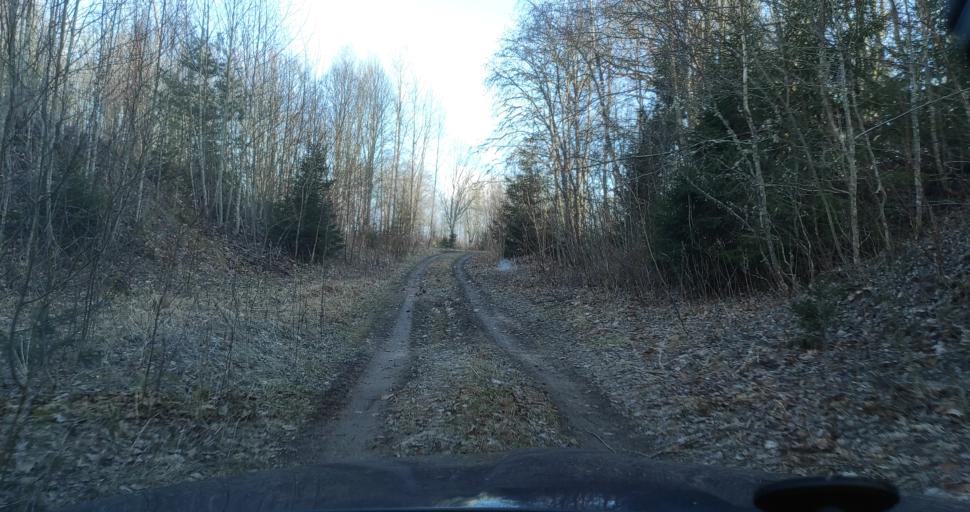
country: LV
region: Aizpute
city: Aizpute
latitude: 56.8736
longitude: 21.7563
